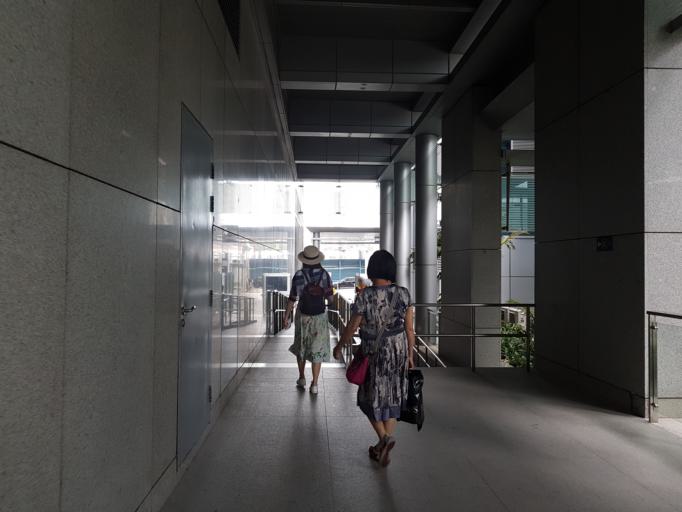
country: SG
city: Singapore
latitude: 1.2651
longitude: 103.8188
